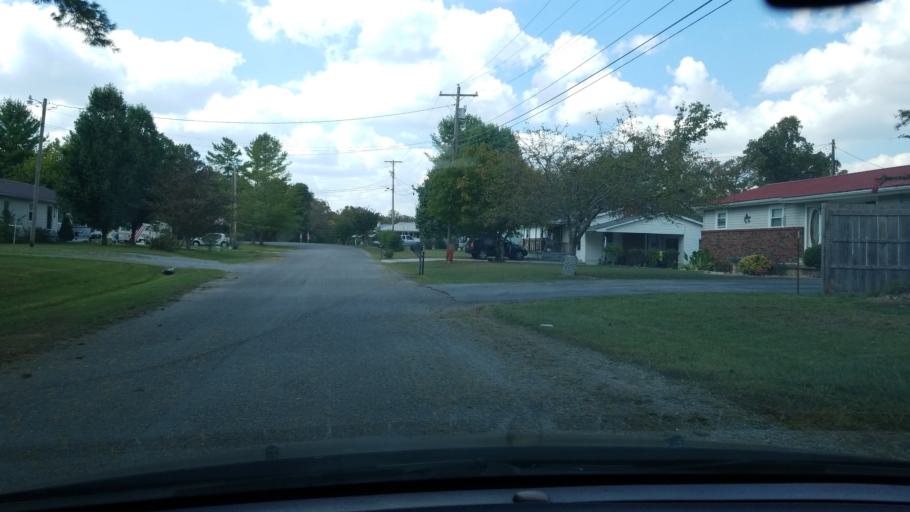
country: US
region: Tennessee
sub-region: Cumberland County
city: Crossville
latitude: 35.9645
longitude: -85.0677
